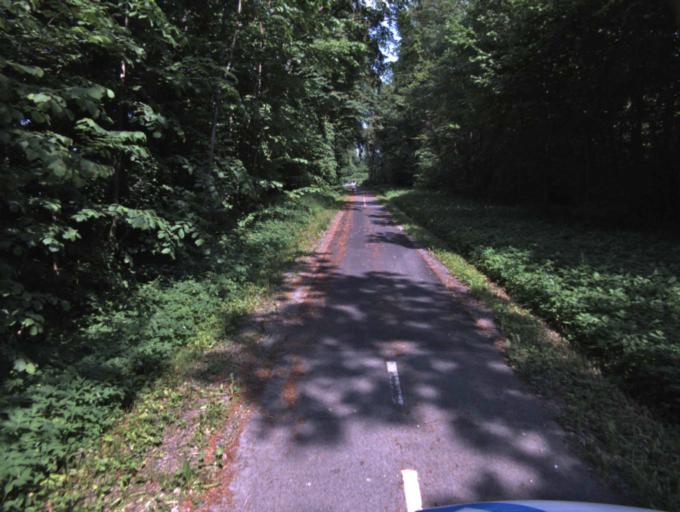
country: SE
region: Skane
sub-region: Kristianstads Kommun
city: Fjalkinge
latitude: 56.0843
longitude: 14.2286
